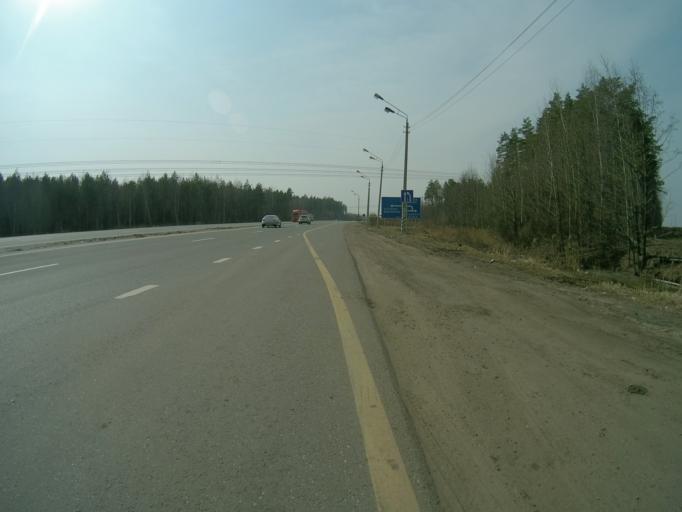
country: RU
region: Vladimir
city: Kommunar
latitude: 56.0608
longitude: 40.4521
